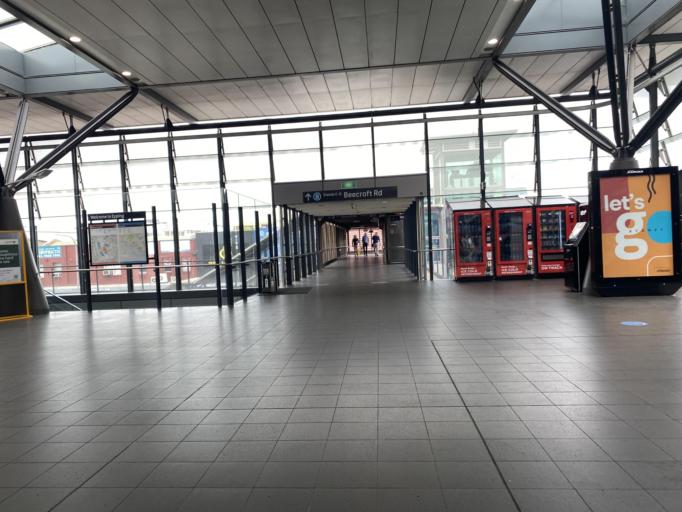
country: AU
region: New South Wales
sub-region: Parramatta
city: Epping
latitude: -33.7726
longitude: 151.0822
